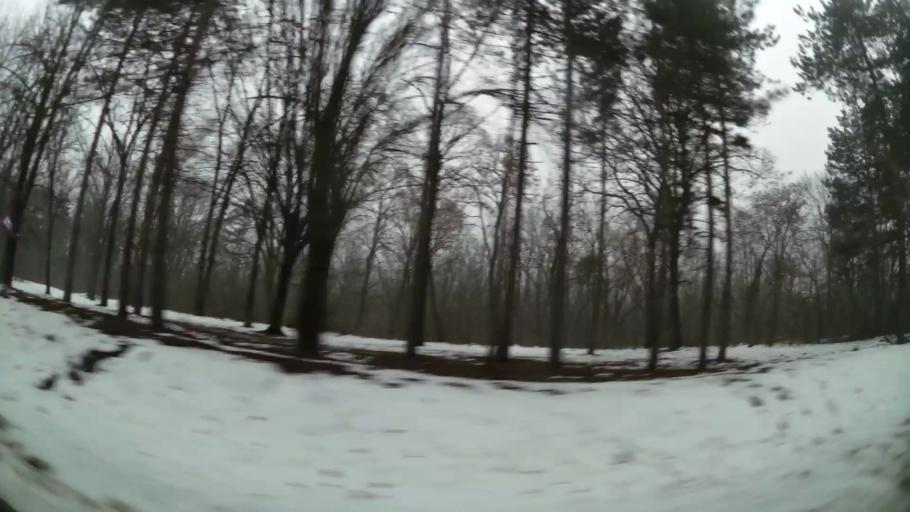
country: RS
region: Central Serbia
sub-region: Belgrade
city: Cukarica
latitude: 44.7769
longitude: 20.4302
